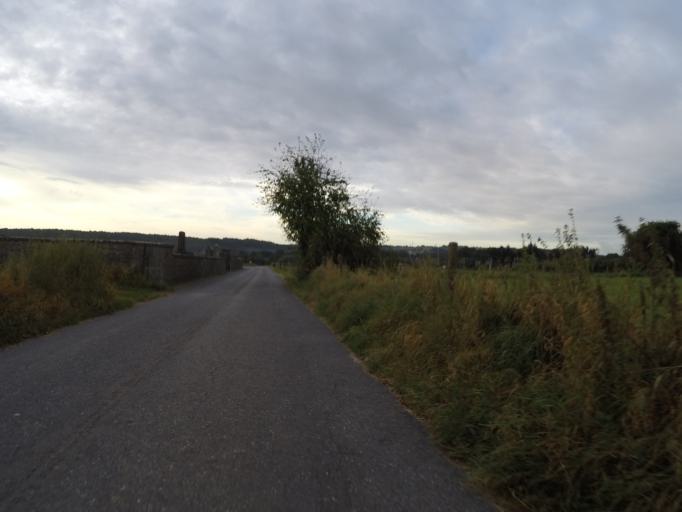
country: BE
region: Wallonia
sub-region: Province de Namur
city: Ciney
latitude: 50.3325
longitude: 5.0648
